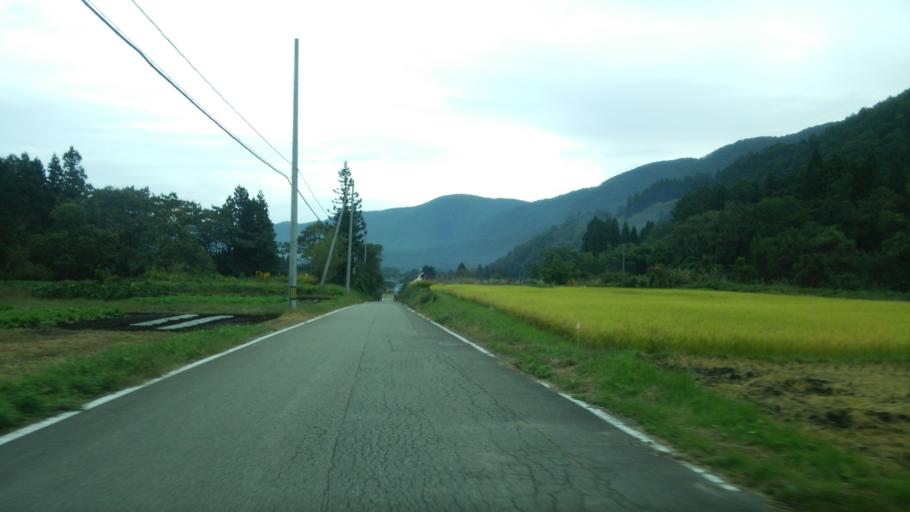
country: JP
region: Fukushima
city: Inawashiro
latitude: 37.3765
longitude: 139.9245
